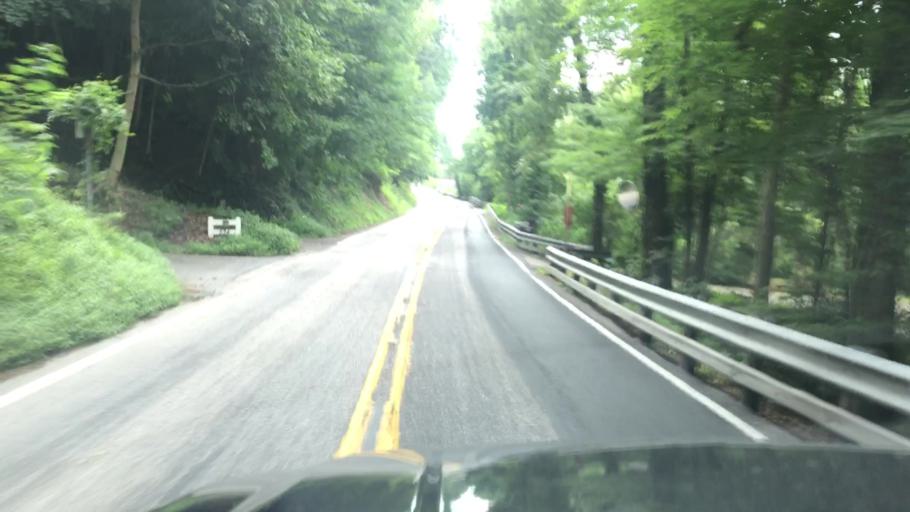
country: US
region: Pennsylvania
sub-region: Cumberland County
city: Shiremanstown
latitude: 40.2516
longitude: -76.9739
